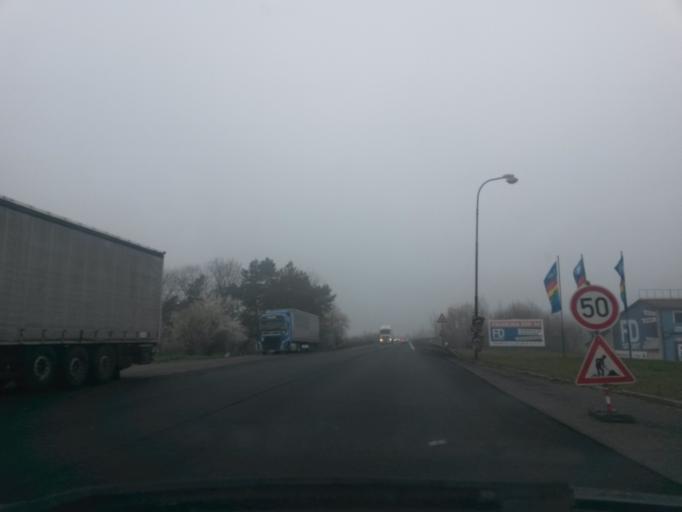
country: CZ
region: Ustecky
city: Cerncice
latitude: 50.3321
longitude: 13.8403
